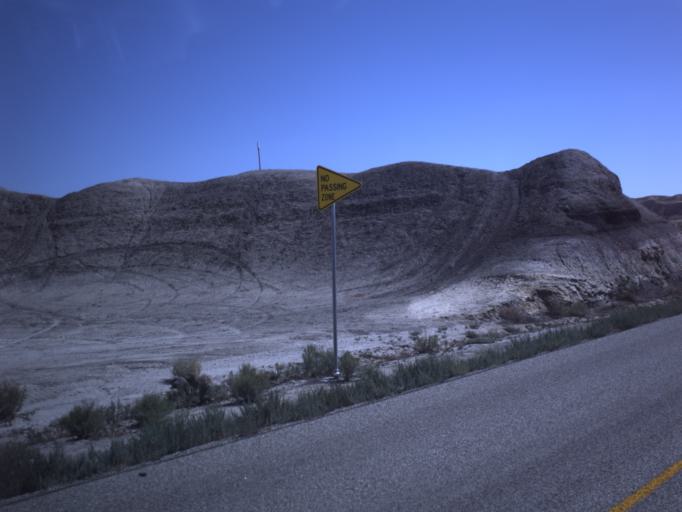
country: US
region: Utah
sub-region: Wayne County
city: Loa
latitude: 38.3652
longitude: -110.9127
